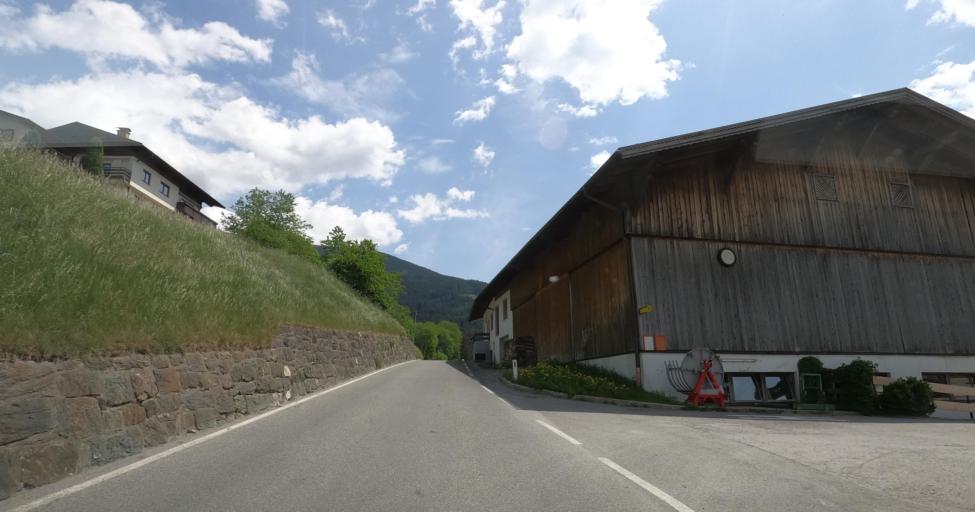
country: AT
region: Tyrol
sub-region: Politischer Bezirk Innsbruck Land
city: Ellbogen
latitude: 47.1652
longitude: 11.4494
